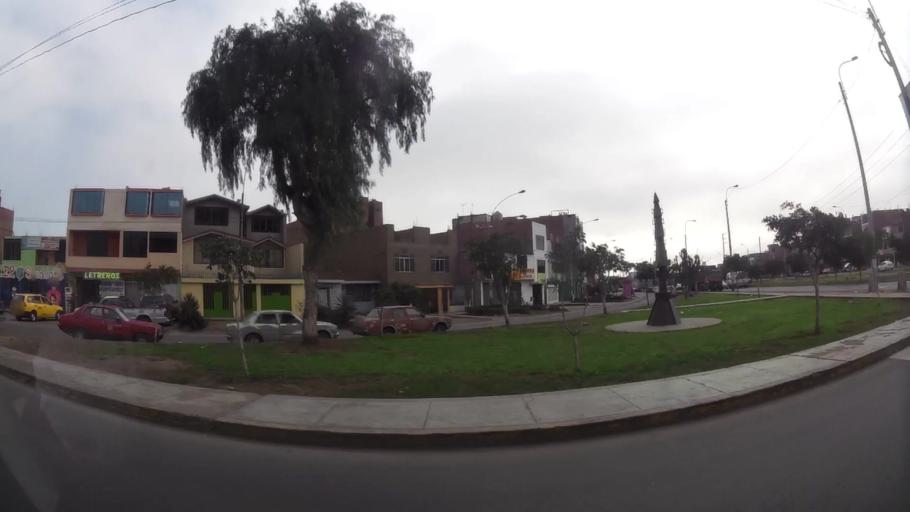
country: PE
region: Lima
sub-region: Lima
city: Independencia
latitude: -12.0123
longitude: -77.0873
